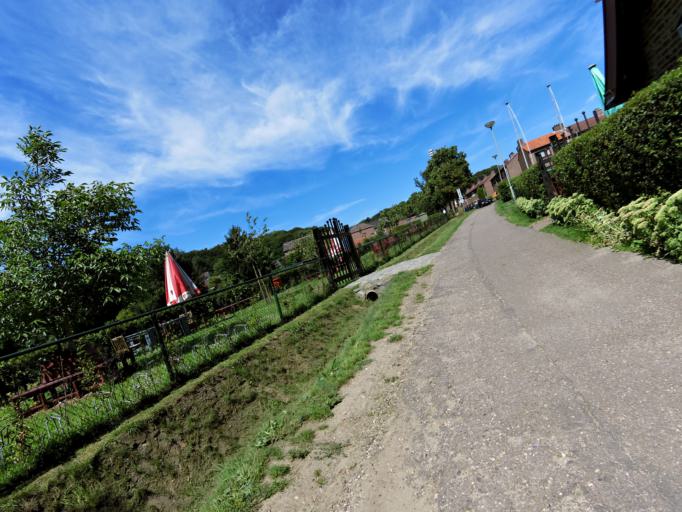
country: DE
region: North Rhine-Westphalia
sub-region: Regierungsbezirk Koln
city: Ubach-Palenberg
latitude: 50.9101
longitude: 6.0821
